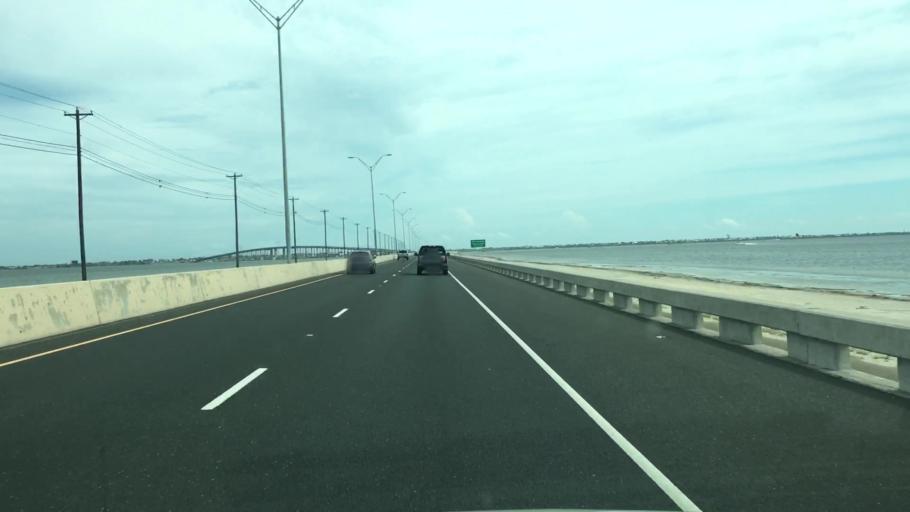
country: US
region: Texas
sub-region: Nueces County
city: Corpus Christi
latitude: 27.6479
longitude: -97.2521
